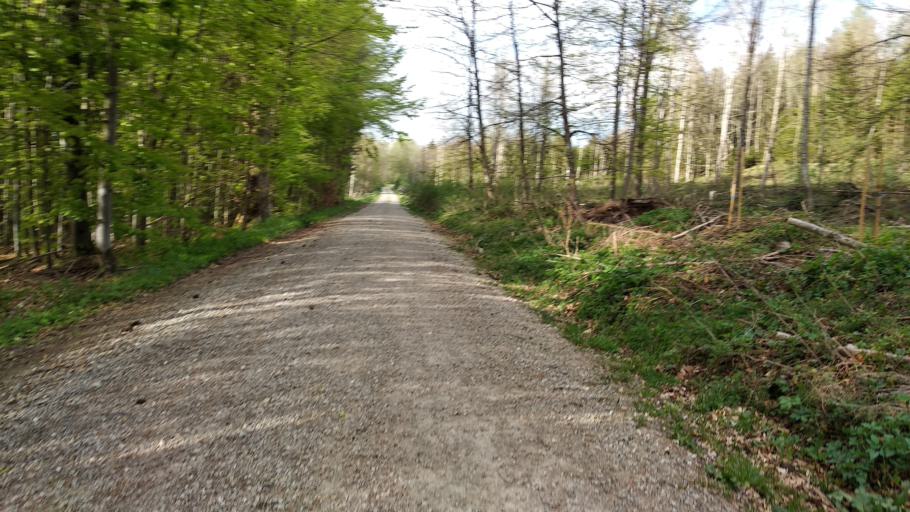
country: DE
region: Bavaria
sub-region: Swabia
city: Woringen
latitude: 47.9295
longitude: 10.1873
